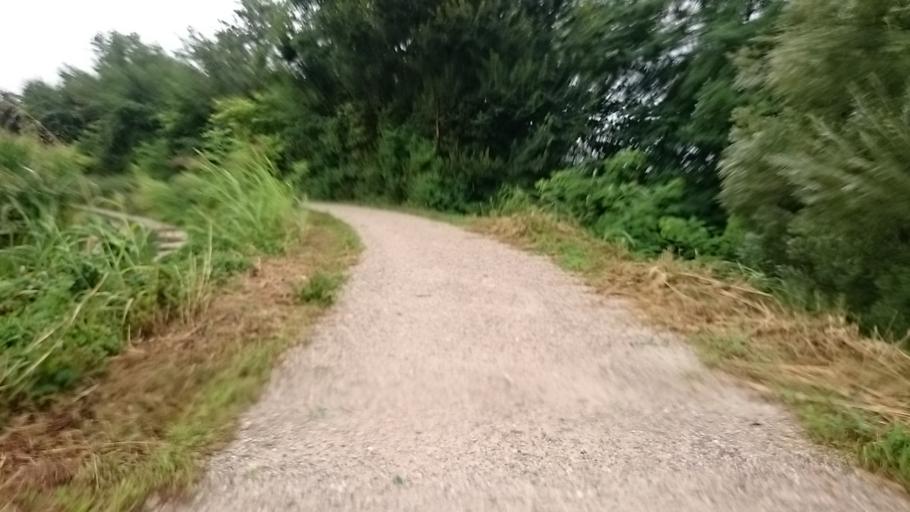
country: IT
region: Veneto
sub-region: Provincia di Treviso
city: Villa d'Asolo
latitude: 45.7757
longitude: 11.8876
